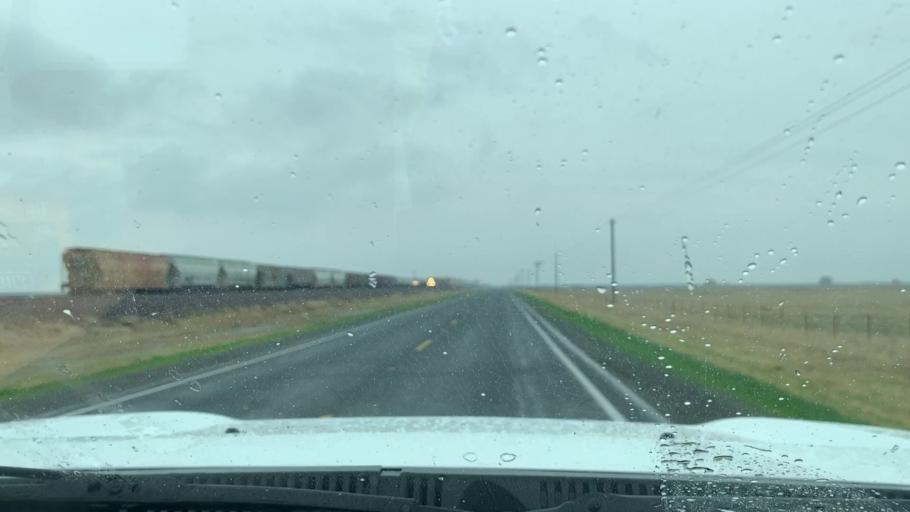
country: US
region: California
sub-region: Tulare County
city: Alpaugh
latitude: 35.9091
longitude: -119.4182
